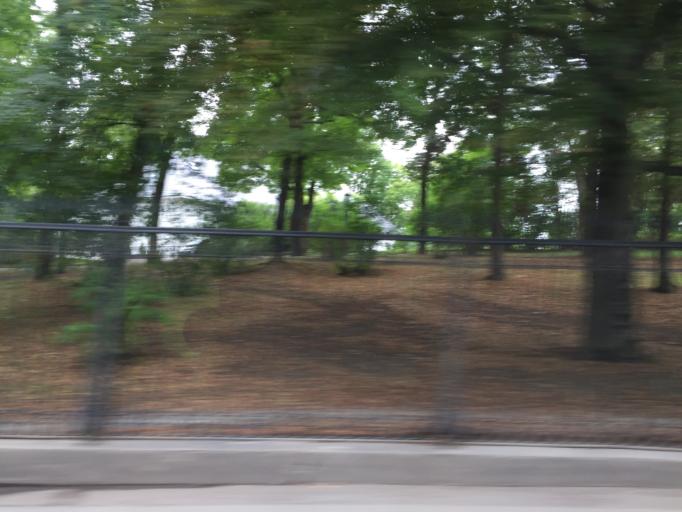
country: NO
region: Oslo
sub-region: Oslo
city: Sjolyststranda
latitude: 59.9111
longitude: 10.6791
